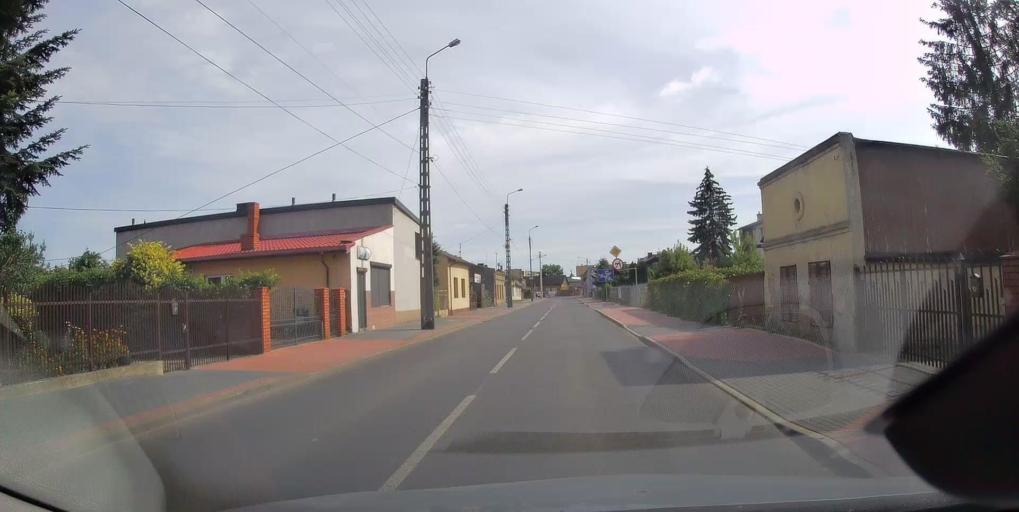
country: PL
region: Lodz Voivodeship
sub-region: Powiat tomaszowski
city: Tomaszow Mazowiecki
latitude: 51.5264
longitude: 19.9974
